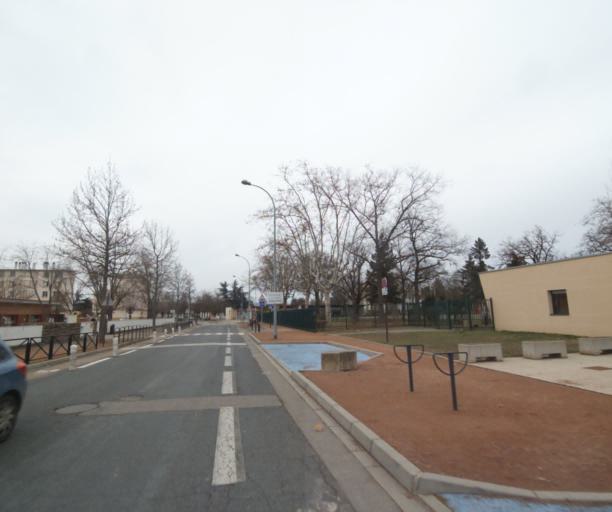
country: FR
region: Rhone-Alpes
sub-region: Departement de la Loire
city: Le Coteau
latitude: 46.0567
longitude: 4.0915
